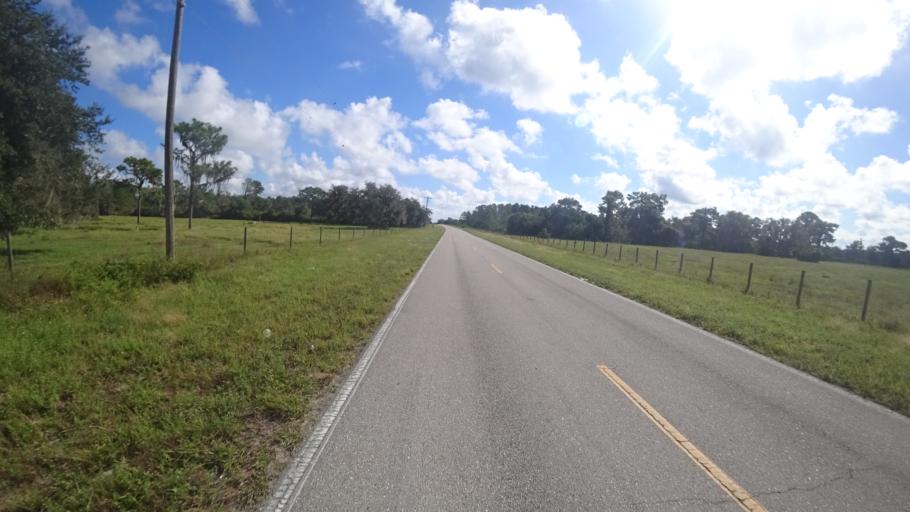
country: US
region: Florida
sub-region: Sarasota County
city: Lake Sarasota
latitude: 27.3392
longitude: -82.1962
